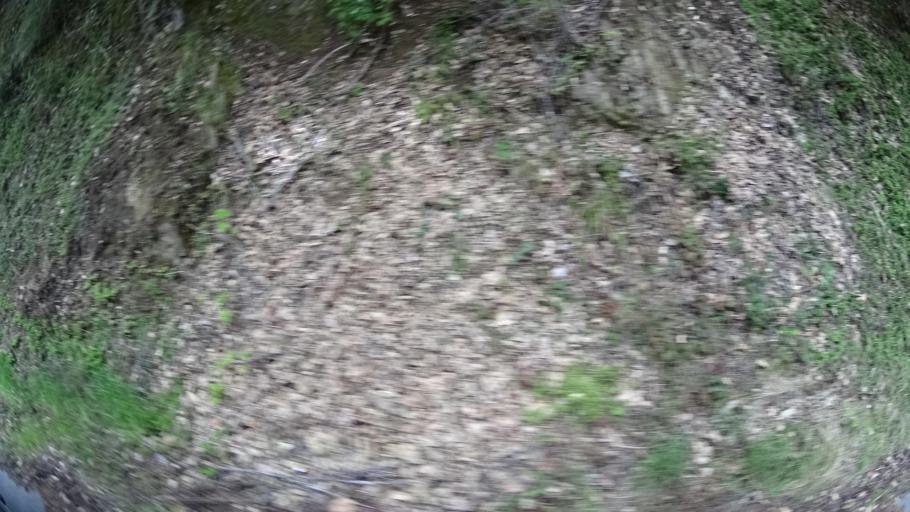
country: US
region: California
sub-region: Humboldt County
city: Blue Lake
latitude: 40.7583
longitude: -123.9133
